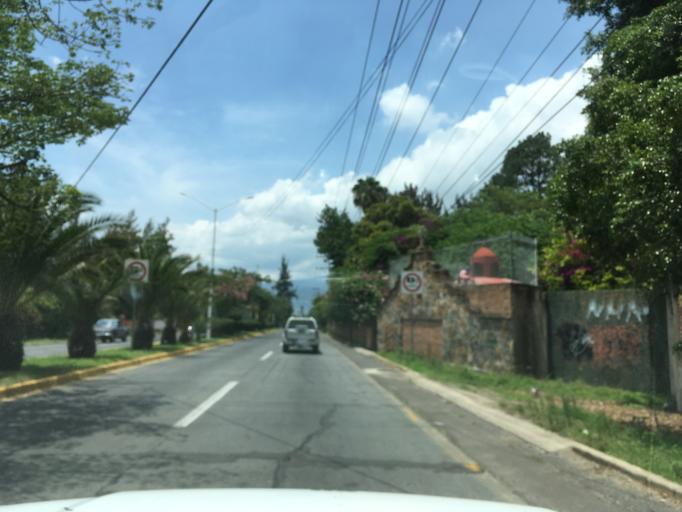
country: MX
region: Jalisco
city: Tlajomulco de Zuniga
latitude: 20.4842
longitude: -103.4568
